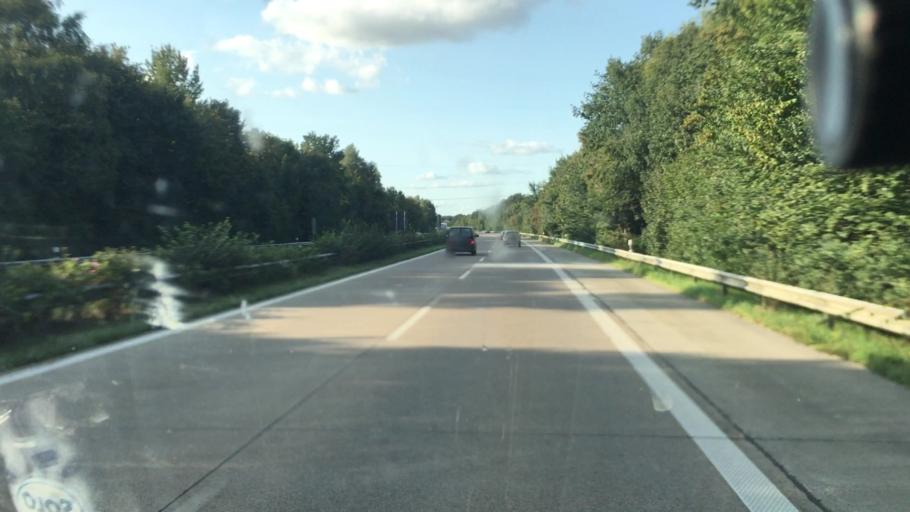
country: DE
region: Lower Saxony
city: Rastede
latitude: 53.2505
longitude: 8.1743
